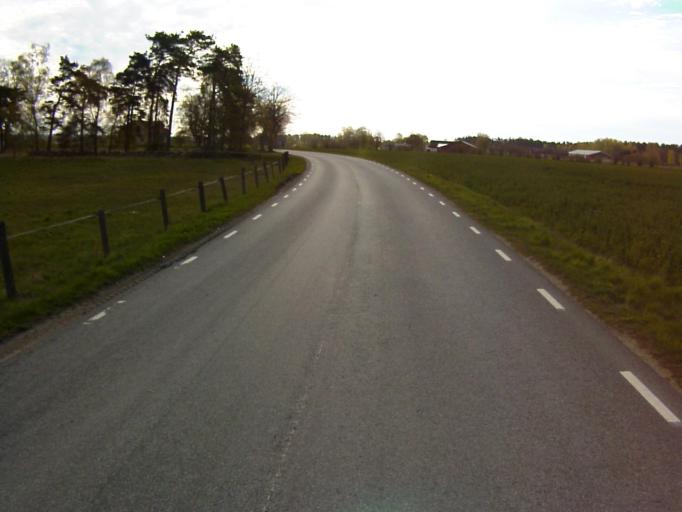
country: SE
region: Skane
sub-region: Kristianstads Kommun
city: Norra Asum
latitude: 55.9929
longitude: 14.1232
